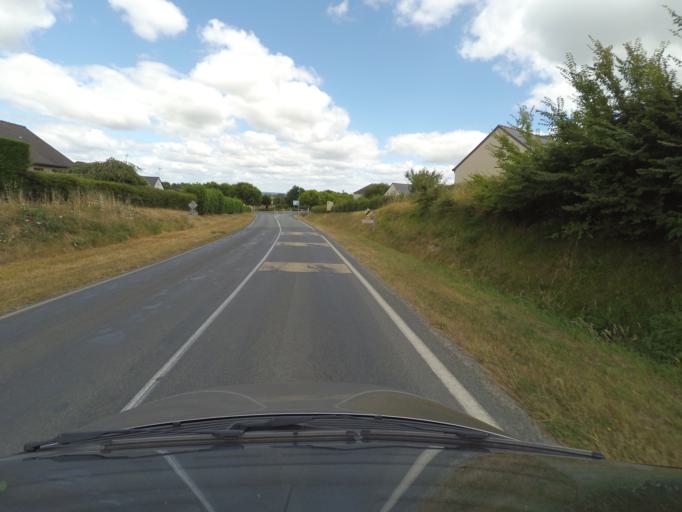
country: FR
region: Pays de la Loire
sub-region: Departement de Maine-et-Loire
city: Gennes
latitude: 47.3335
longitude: -0.2341
